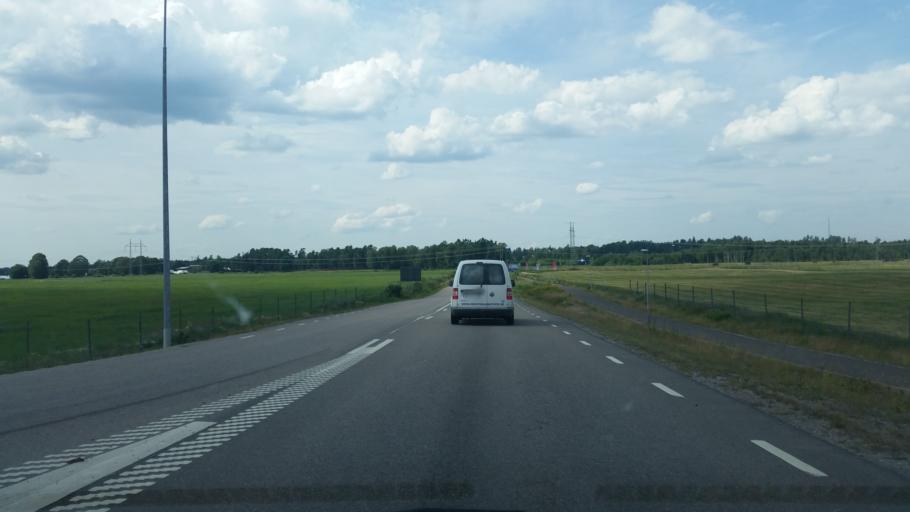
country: SE
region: Vaestra Goetaland
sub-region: Skara Kommun
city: Axvall
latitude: 58.3983
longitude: 13.5614
